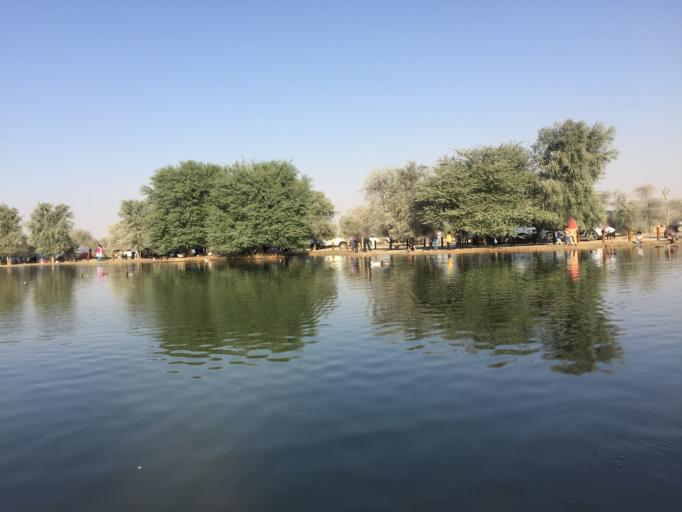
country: AE
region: Dubai
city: Dubai
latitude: 24.8446
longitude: 55.3516
